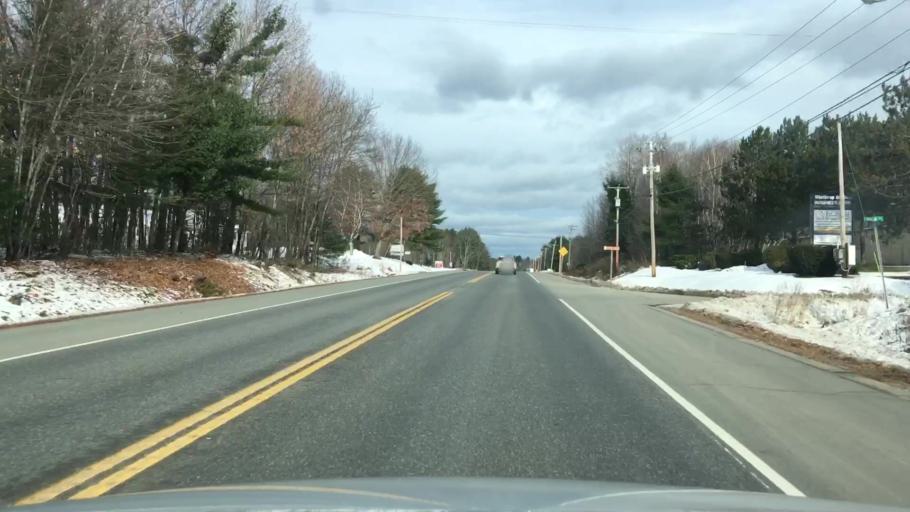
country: US
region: Maine
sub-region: Kennebec County
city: Winthrop
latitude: 44.2831
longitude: -70.0011
